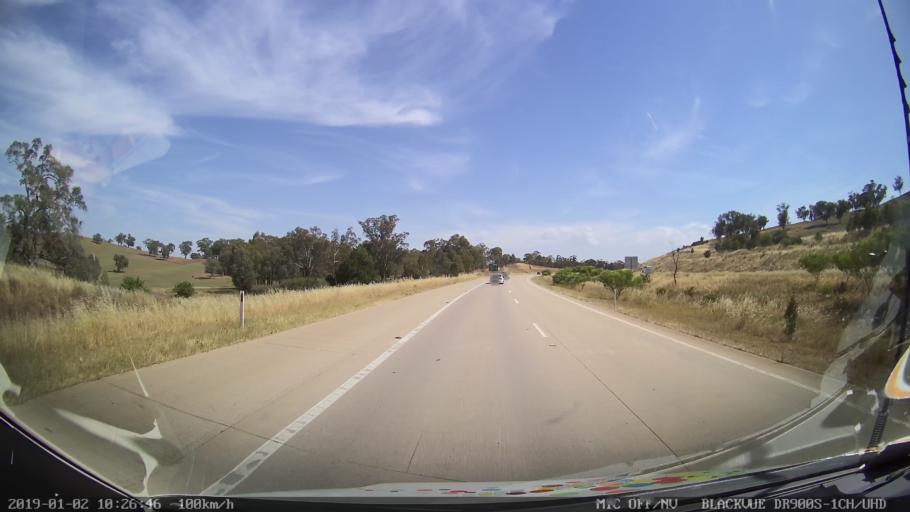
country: AU
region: New South Wales
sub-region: Gundagai
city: Gundagai
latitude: -34.9163
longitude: 148.1684
